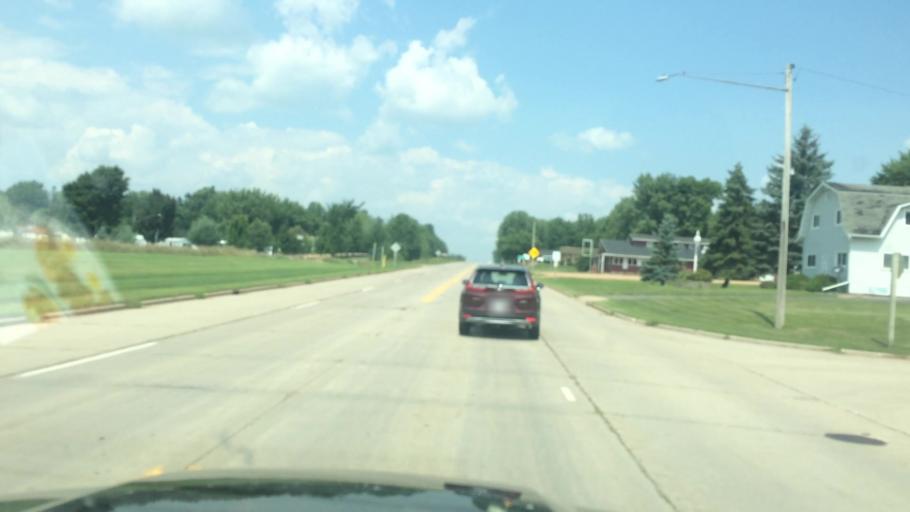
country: US
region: Wisconsin
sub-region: Clark County
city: Colby
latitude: 44.8450
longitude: -90.3160
